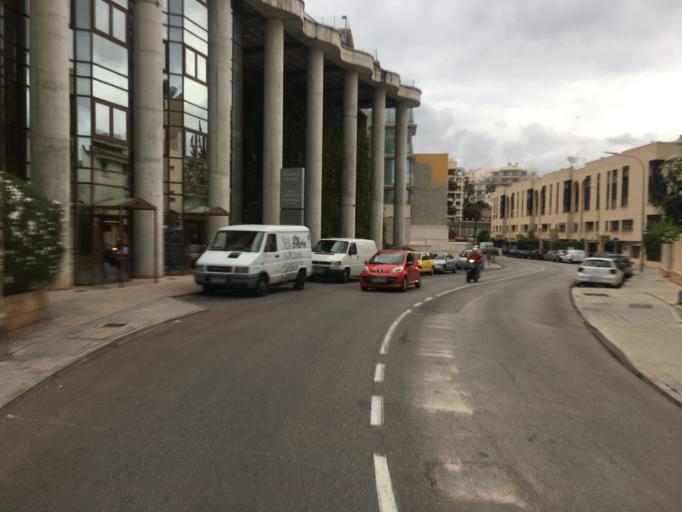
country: ES
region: Balearic Islands
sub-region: Illes Balears
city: Palma
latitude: 39.5565
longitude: 2.6231
